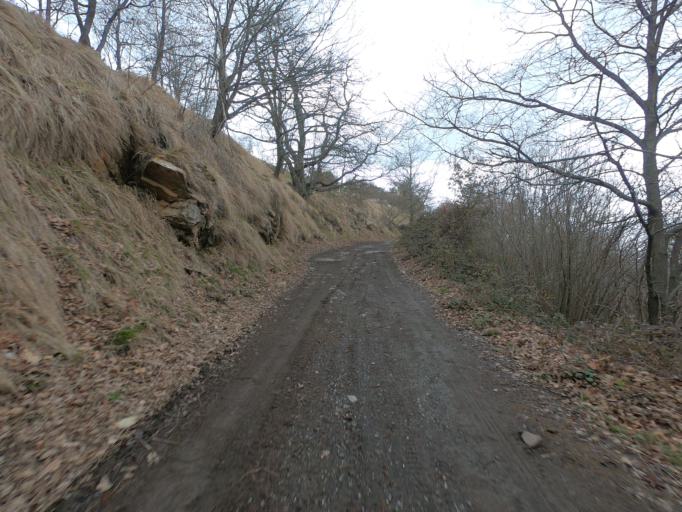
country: IT
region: Liguria
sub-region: Provincia di Imperia
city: Badalucco
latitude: 43.9164
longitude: 7.8796
